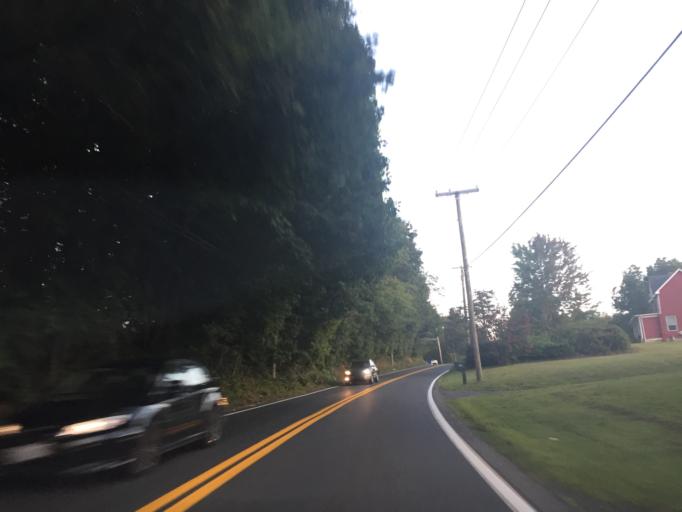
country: US
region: Maryland
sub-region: Harford County
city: Bel Air North
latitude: 39.5915
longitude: -76.3881
